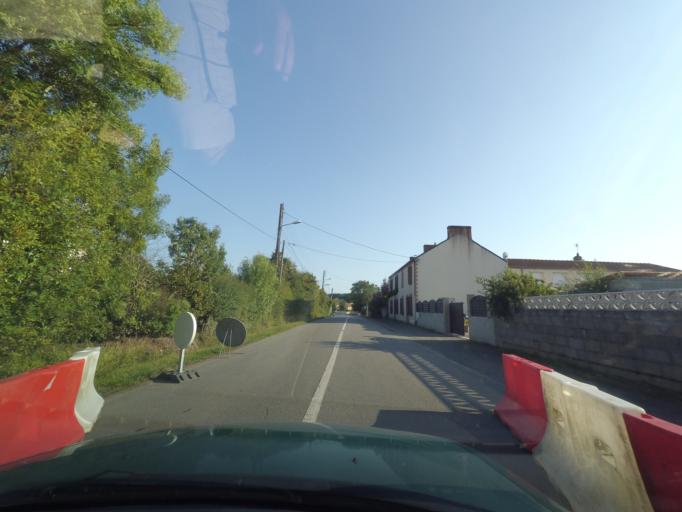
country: FR
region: Pays de la Loire
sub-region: Departement de la Loire-Atlantique
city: La Limouziniere
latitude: 47.0124
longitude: -1.5855
